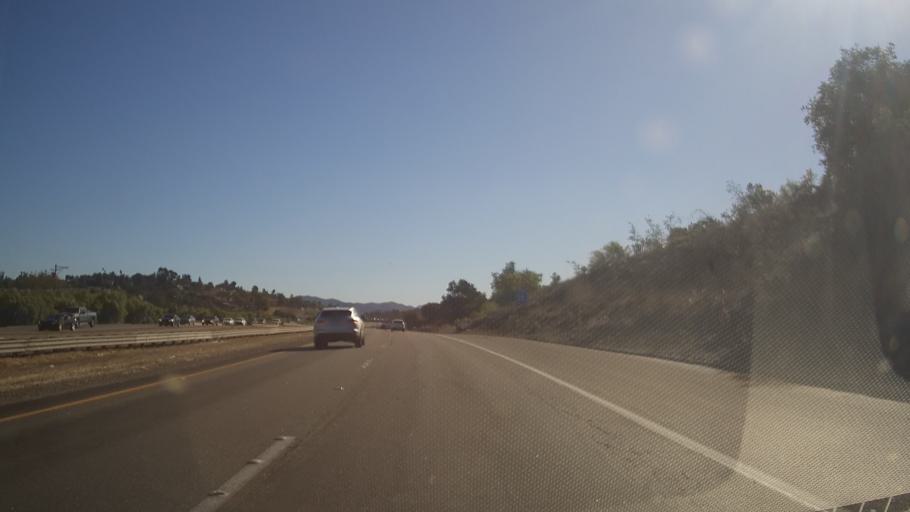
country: US
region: California
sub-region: San Diego County
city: Spring Valley
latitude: 32.7445
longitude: -116.9836
